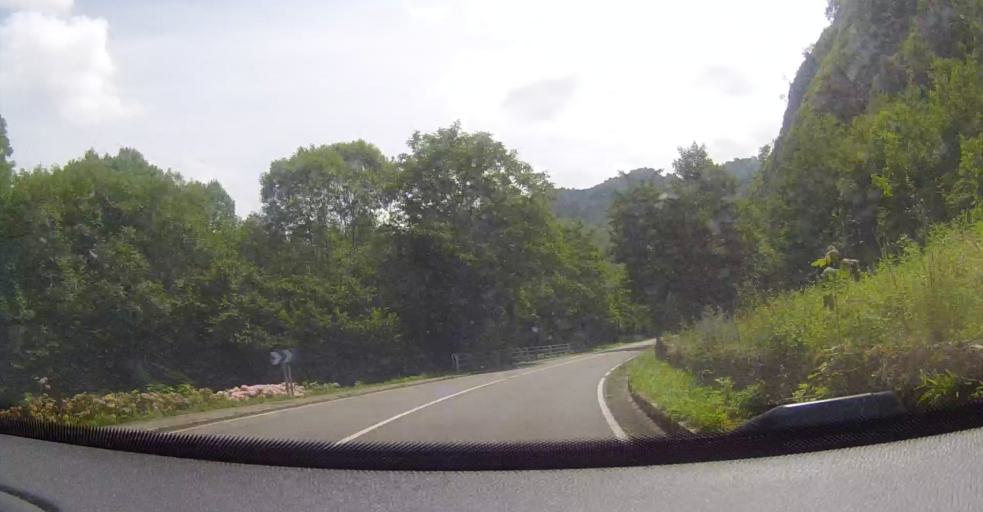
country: ES
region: Asturias
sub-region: Province of Asturias
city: Cangas de Onis
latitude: 43.3197
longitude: -5.0743
